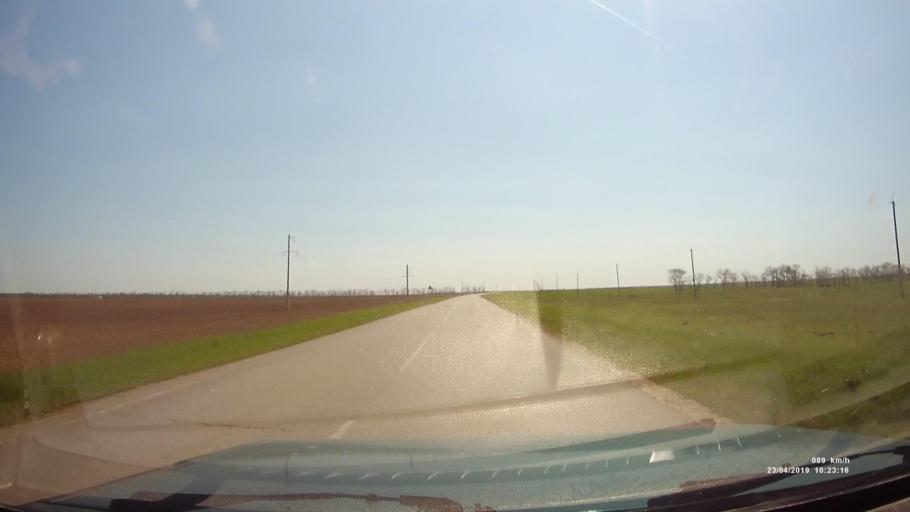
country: RU
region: Rostov
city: Sovetskoye
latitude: 46.6488
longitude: 42.4213
